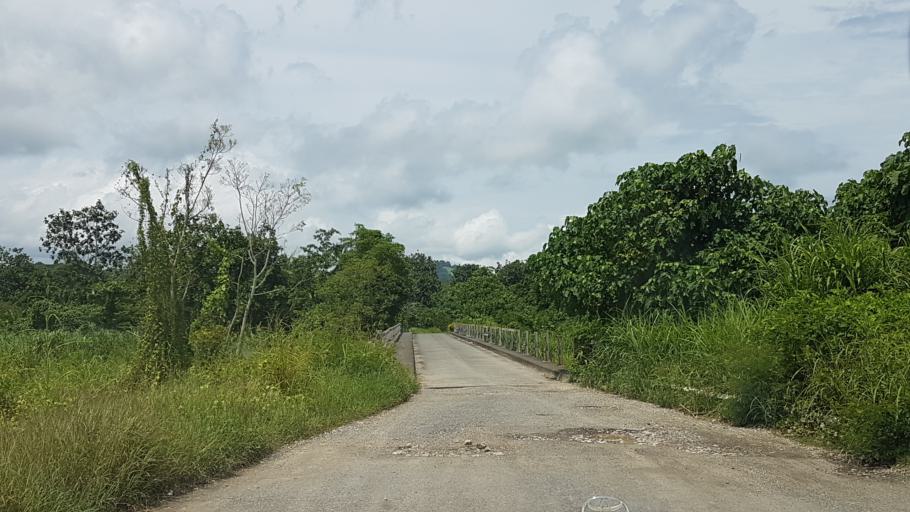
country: PG
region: Madang
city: Madang
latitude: -4.5376
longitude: 145.4811
